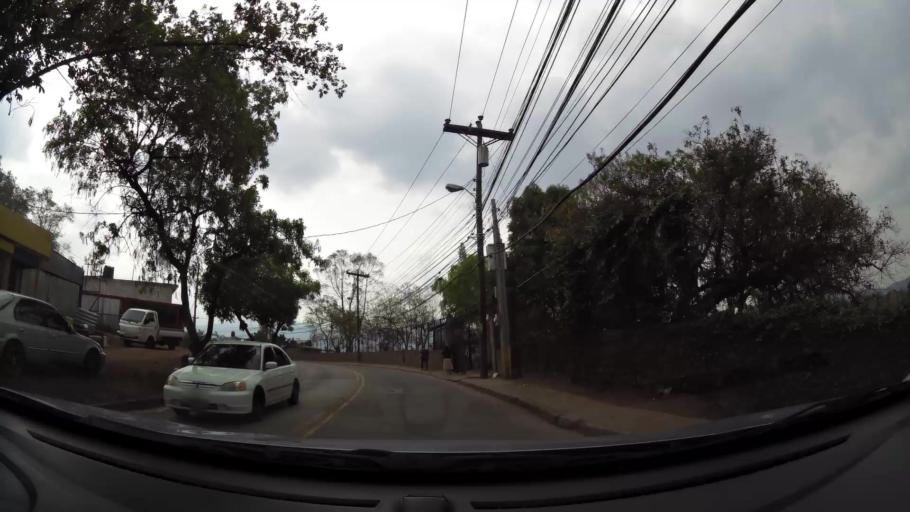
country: HN
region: Francisco Morazan
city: Tegucigalpa
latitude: 14.0905
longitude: -87.1684
